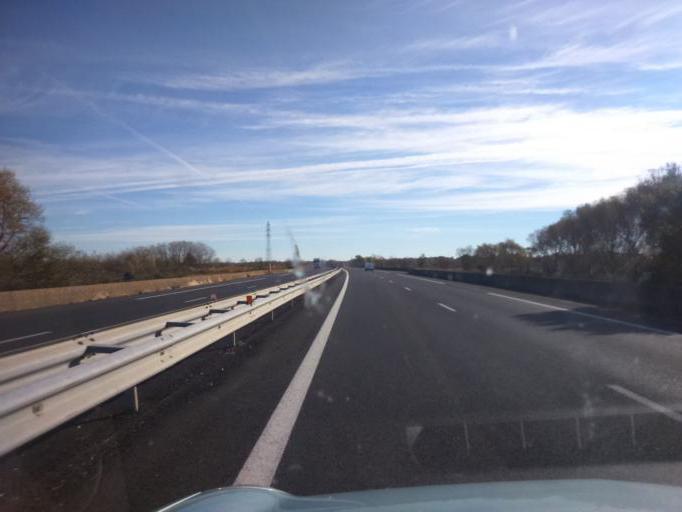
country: FR
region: Poitou-Charentes
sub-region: Departement de la Charente-Maritime
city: Breuil-Magne
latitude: 45.9577
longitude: -0.9356
